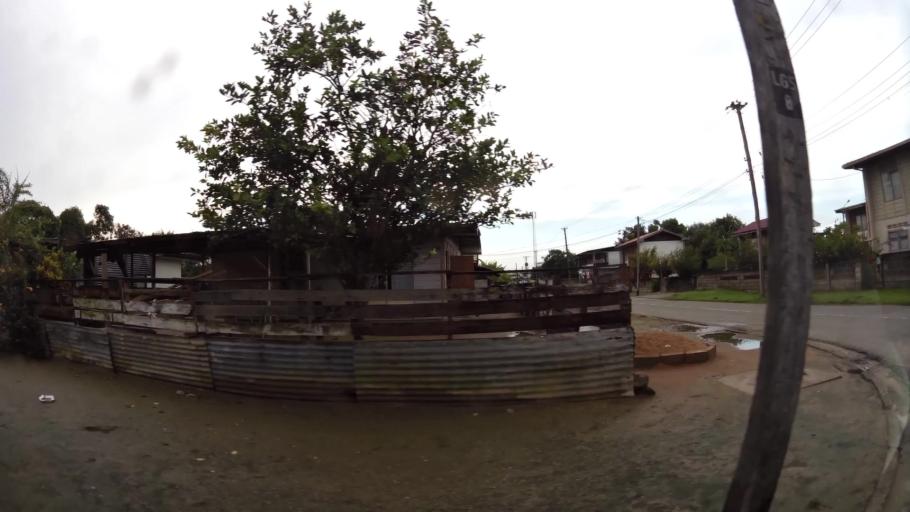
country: SR
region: Paramaribo
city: Paramaribo
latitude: 5.8126
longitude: -55.2000
